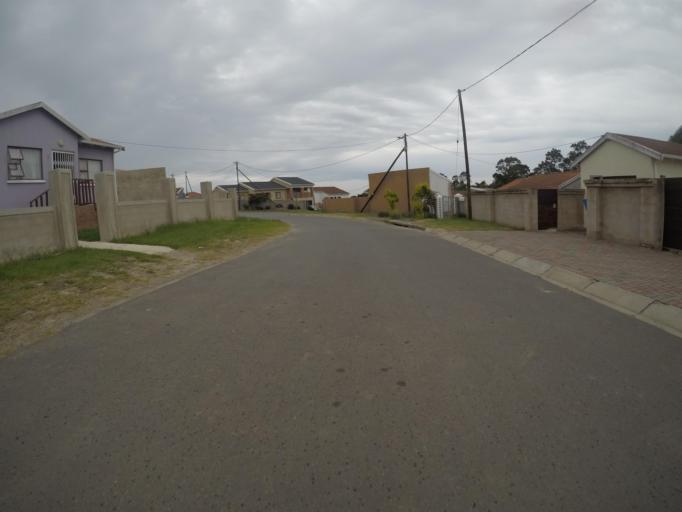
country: ZA
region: Eastern Cape
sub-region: Buffalo City Metropolitan Municipality
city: East London
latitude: -32.9943
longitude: 27.8440
